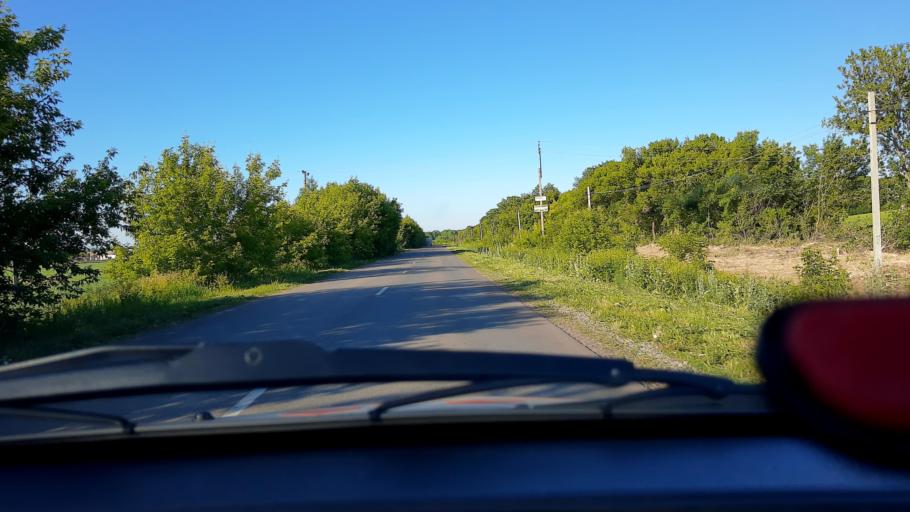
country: RU
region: Bashkortostan
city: Kabakovo
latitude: 54.5071
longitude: 55.9309
